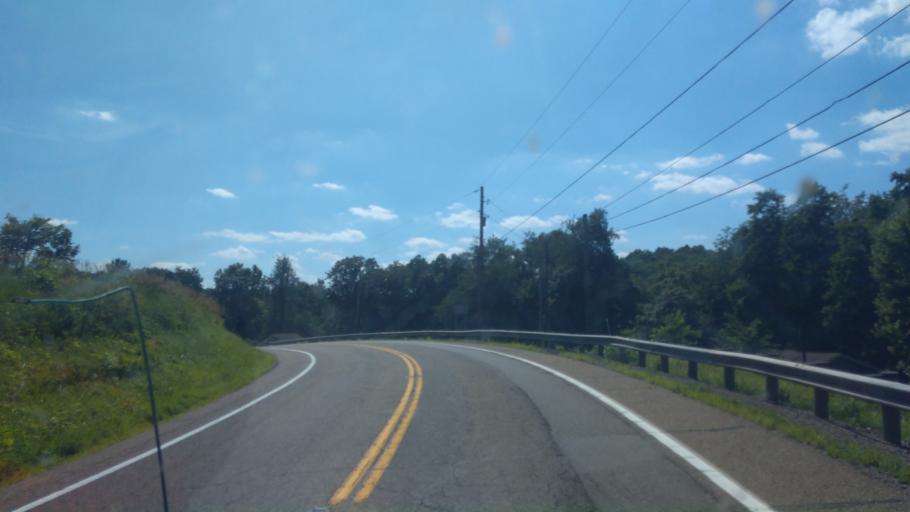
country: US
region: Ohio
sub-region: Carroll County
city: Carrollton
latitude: 40.5525
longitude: -81.1568
